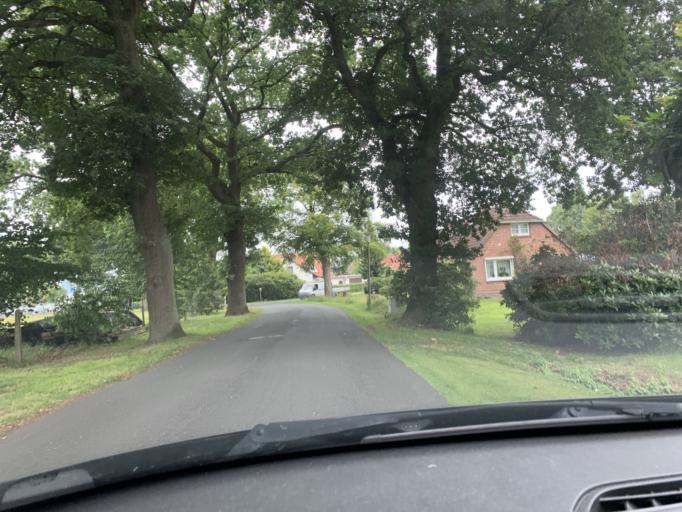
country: DE
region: Lower Saxony
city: Westerstede
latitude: 53.2622
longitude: 7.9448
